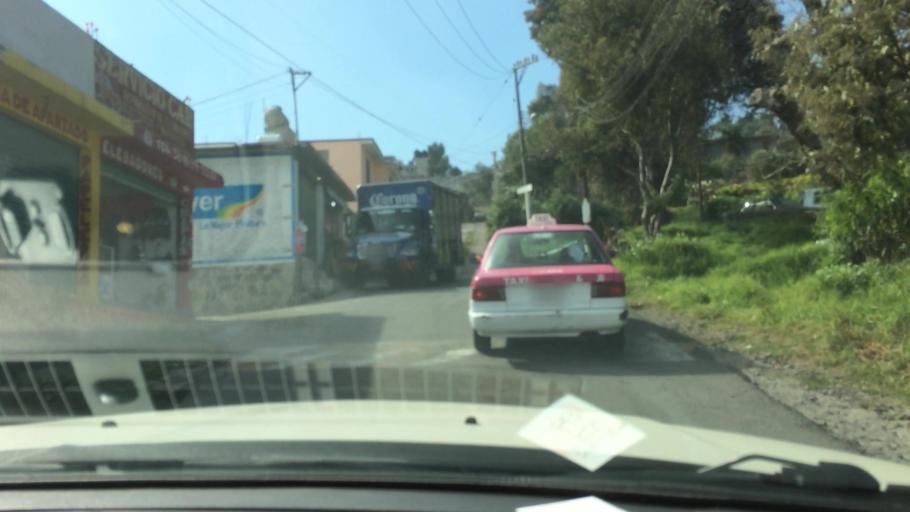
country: MX
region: Mexico City
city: Xochimilco
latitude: 19.2367
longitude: -99.1525
